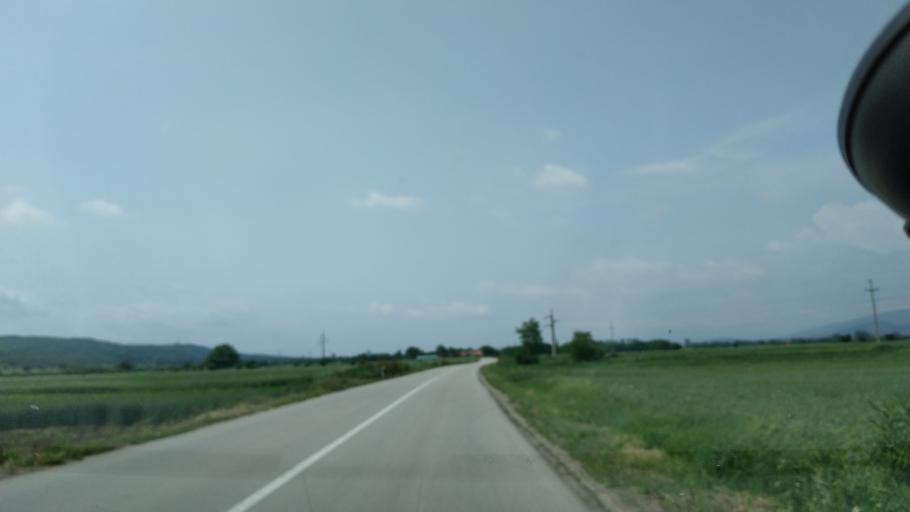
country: RS
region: Central Serbia
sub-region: Nisavski Okrug
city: Aleksinac
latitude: 43.4641
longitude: 21.7299
